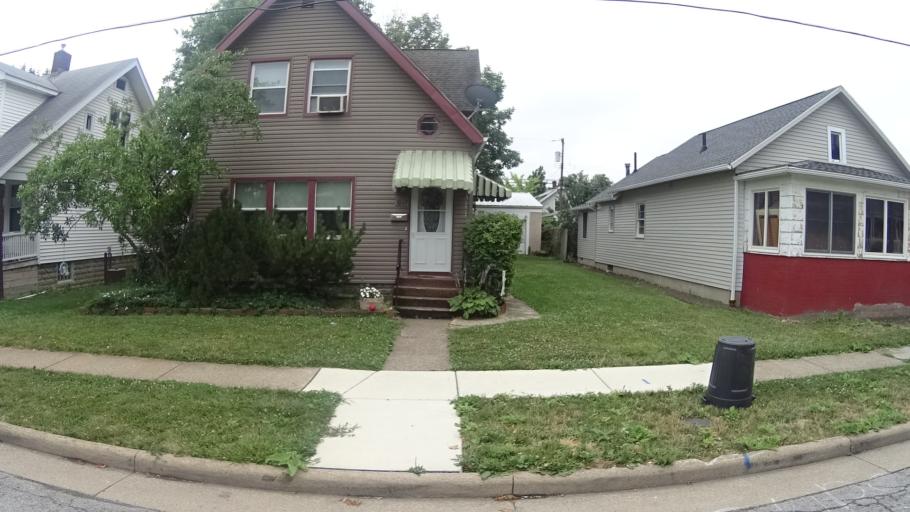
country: US
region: Ohio
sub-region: Erie County
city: Sandusky
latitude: 41.4501
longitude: -82.6955
